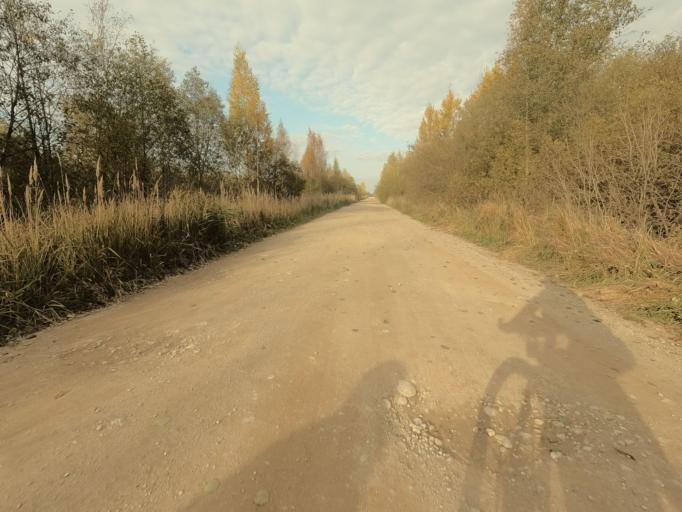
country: RU
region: Novgorod
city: Volkhovskiy
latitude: 58.9040
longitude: 31.0353
